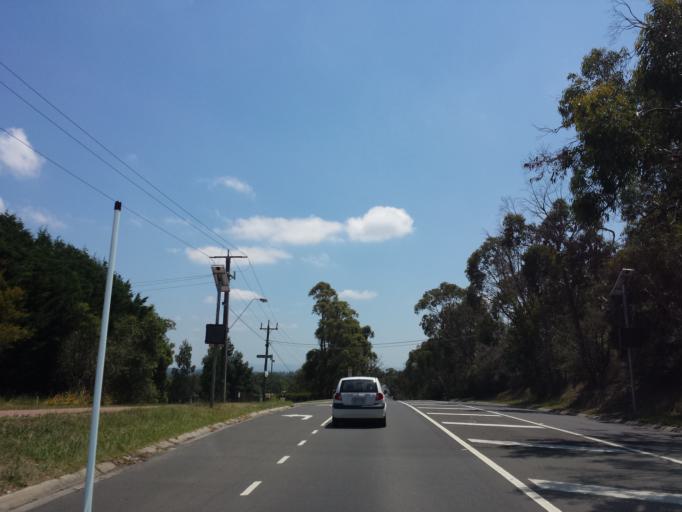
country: AU
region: Victoria
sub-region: Maroondah
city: Kilsyth South
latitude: -37.8303
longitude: 145.3185
